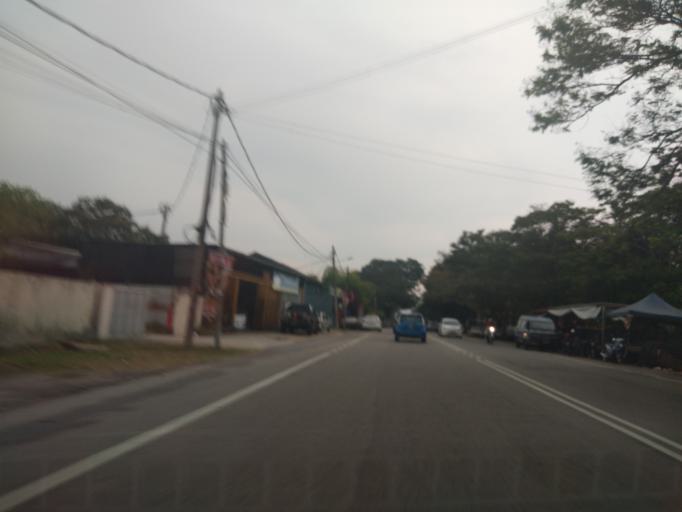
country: MY
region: Penang
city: Permatang Kuching
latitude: 5.4505
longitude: 100.4013
